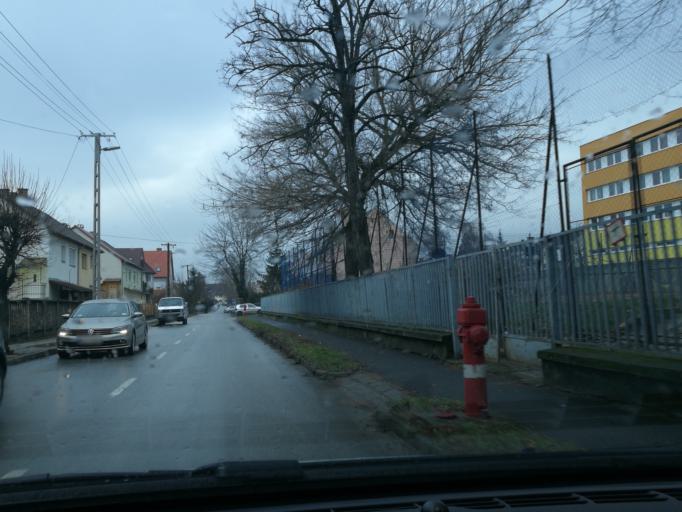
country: HU
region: Szabolcs-Szatmar-Bereg
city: Nyiregyhaza
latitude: 47.9653
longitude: 21.7041
